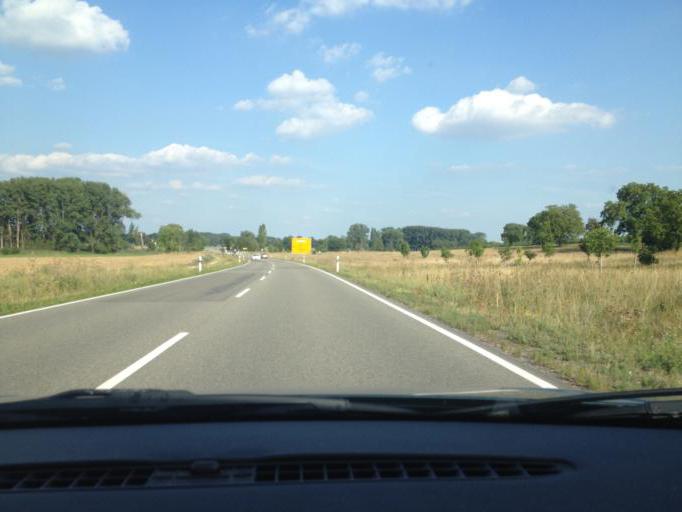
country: DE
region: Rheinland-Pfalz
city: Gommersheim
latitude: 49.3106
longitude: 8.2462
